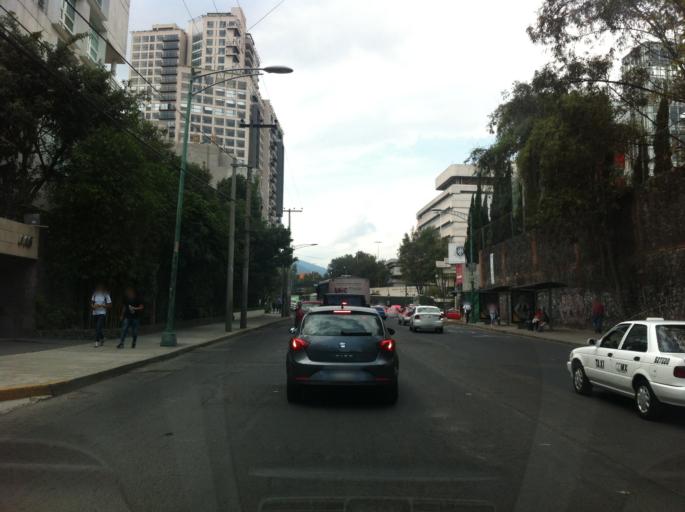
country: MX
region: Mexico City
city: Magdalena Contreras
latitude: 19.3371
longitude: -99.1979
